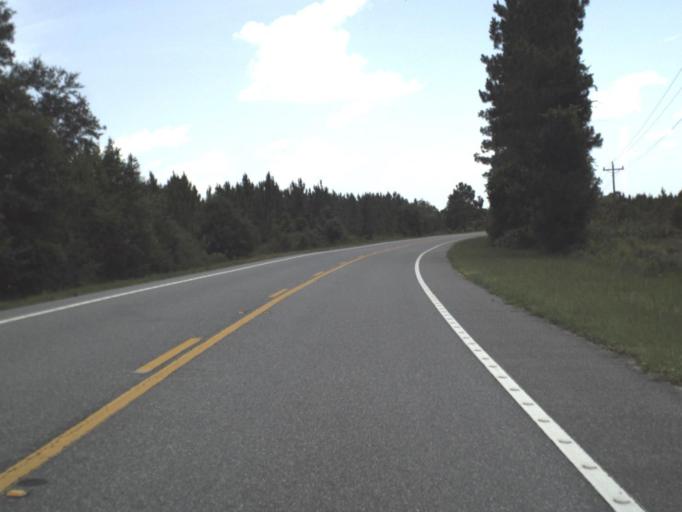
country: US
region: Florida
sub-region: Taylor County
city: Steinhatchee
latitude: 29.7579
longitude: -83.3496
